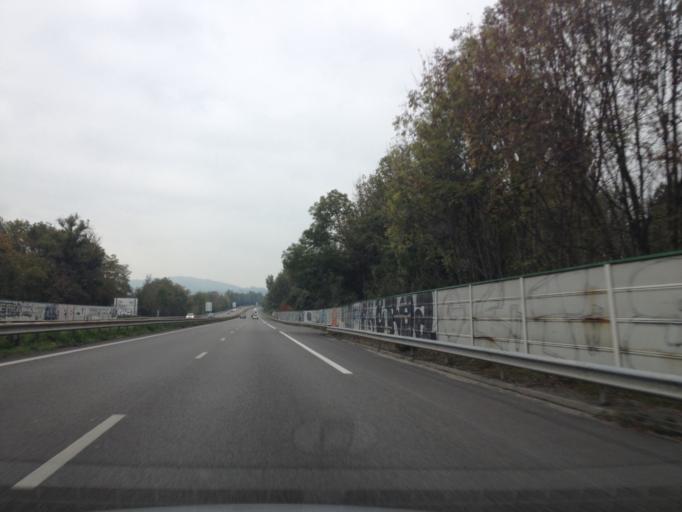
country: FR
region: Rhone-Alpes
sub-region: Departement de la Savoie
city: Gresy-sur-Aix
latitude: 45.7254
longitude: 5.9240
